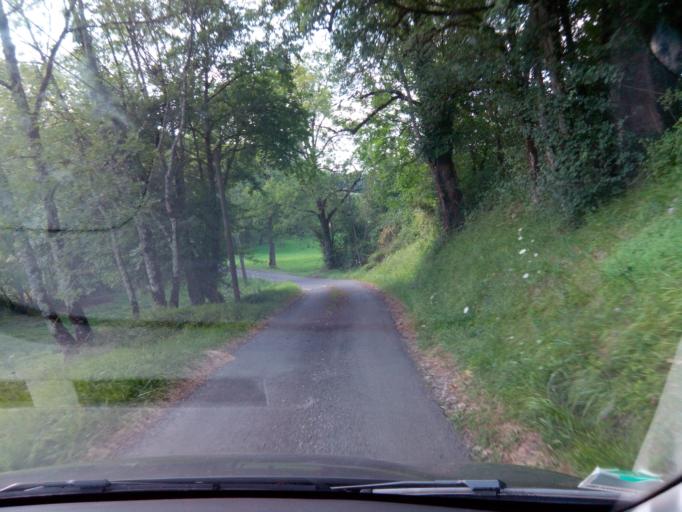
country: FR
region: Limousin
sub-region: Departement de la Correze
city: Cosnac
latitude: 45.0617
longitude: 1.5780
